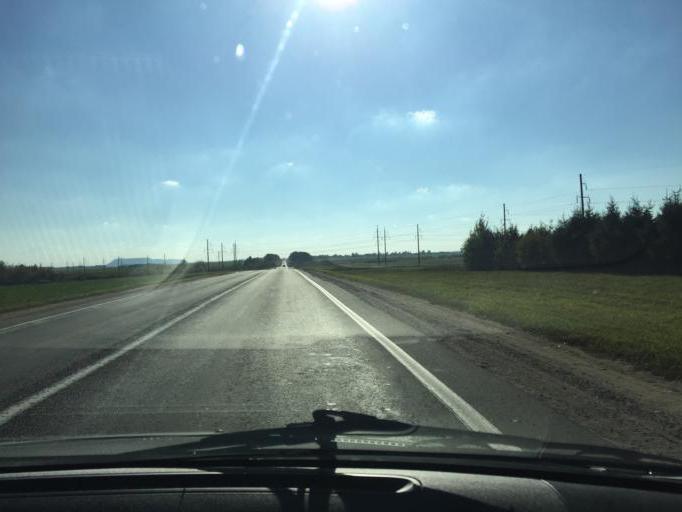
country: BY
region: Minsk
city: Slutsk
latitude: 52.9819
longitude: 27.5044
